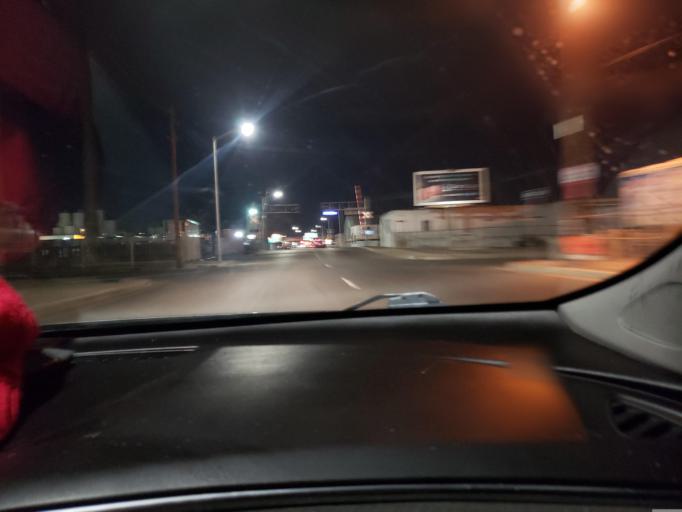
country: US
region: New Mexico
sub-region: Bernalillo County
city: Albuquerque
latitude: 35.1016
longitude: -106.6460
